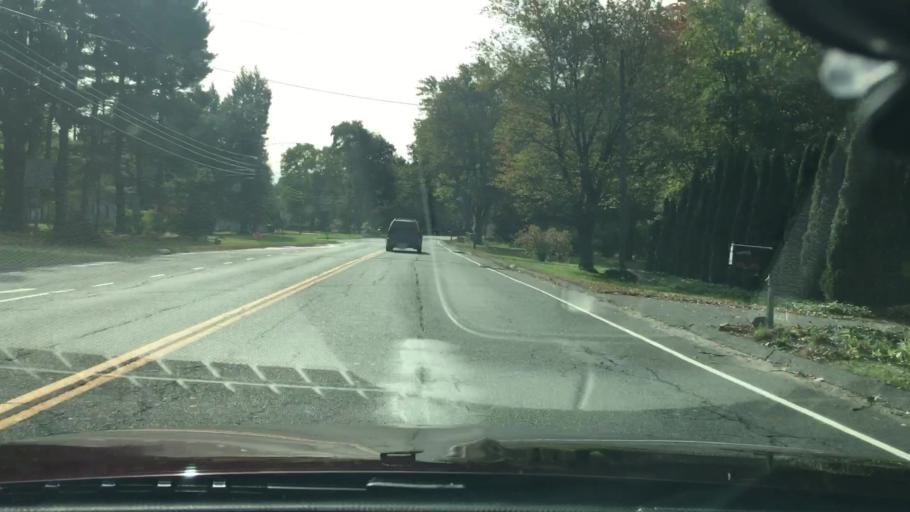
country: US
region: Connecticut
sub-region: Hartford County
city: Plainville
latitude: 41.7024
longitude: -72.8790
